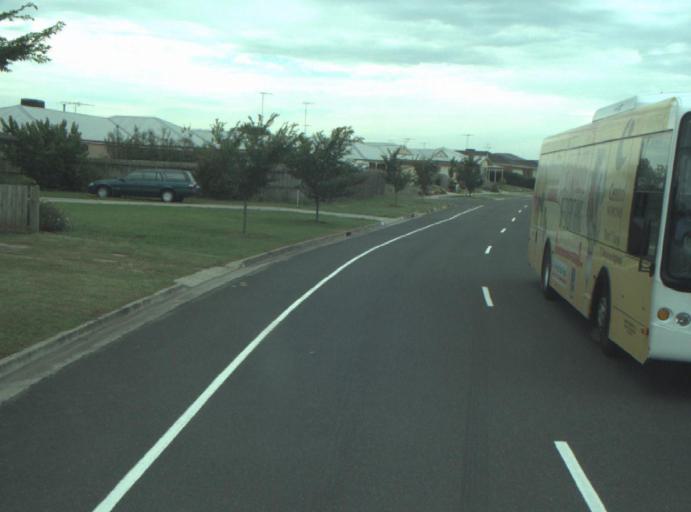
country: AU
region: Victoria
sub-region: Greater Geelong
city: Breakwater
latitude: -38.1948
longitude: 144.3916
